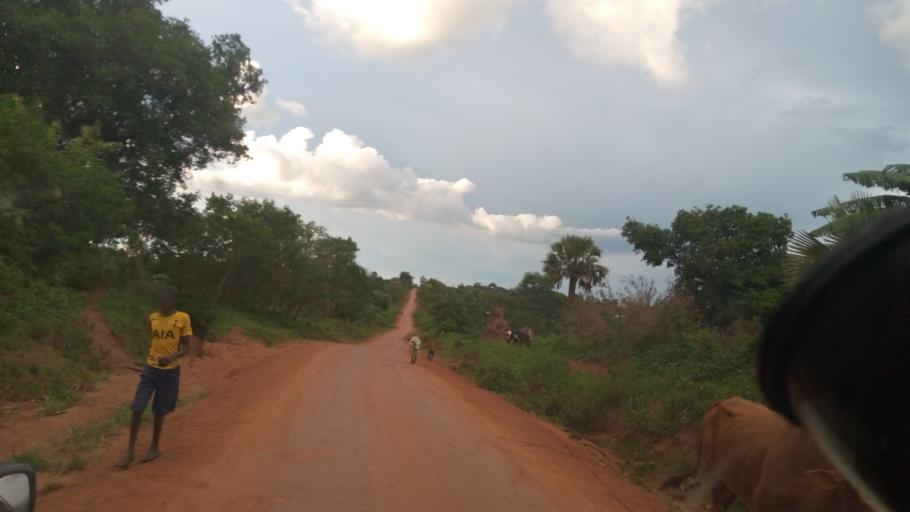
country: UG
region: Northern Region
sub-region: Kole District
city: Kole
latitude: 2.3836
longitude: 32.9326
